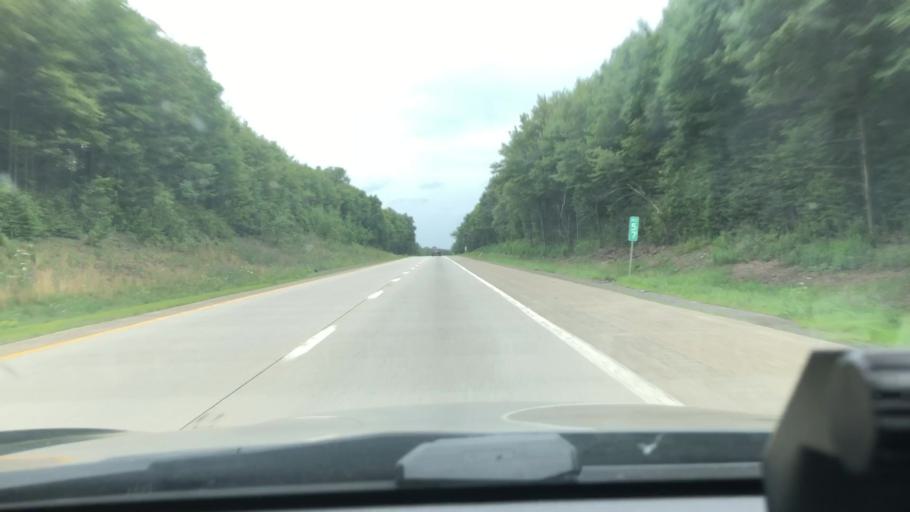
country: US
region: Pennsylvania
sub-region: Monroe County
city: Mount Pocono
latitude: 41.1504
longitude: -75.4092
